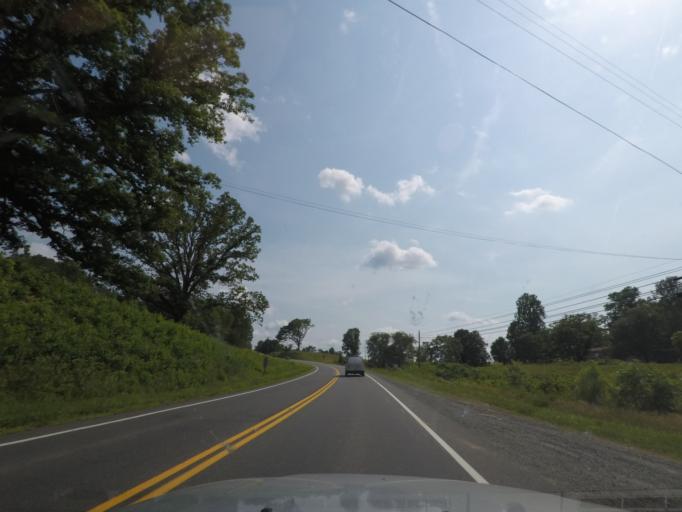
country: US
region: Virginia
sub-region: Fluvanna County
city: Palmyra
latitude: 37.8526
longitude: -78.2712
